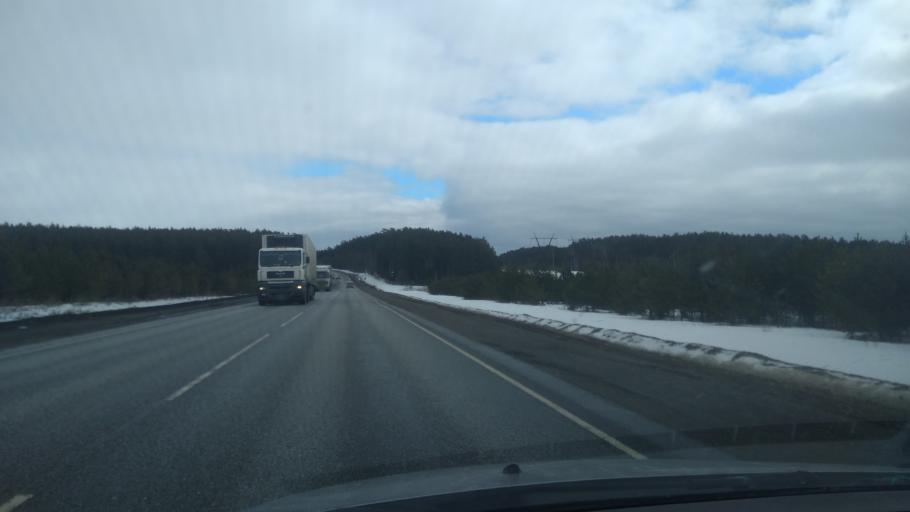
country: RU
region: Sverdlovsk
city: Achit
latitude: 56.7805
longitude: 57.9339
